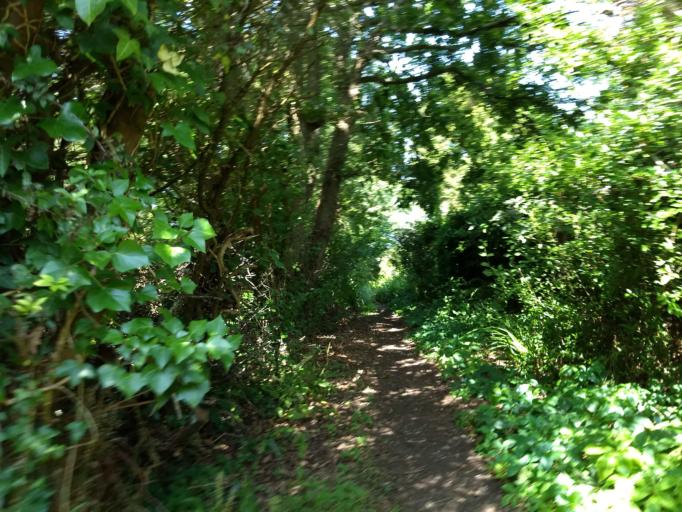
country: GB
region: England
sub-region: Isle of Wight
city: Northwood
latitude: 50.7291
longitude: -1.3238
